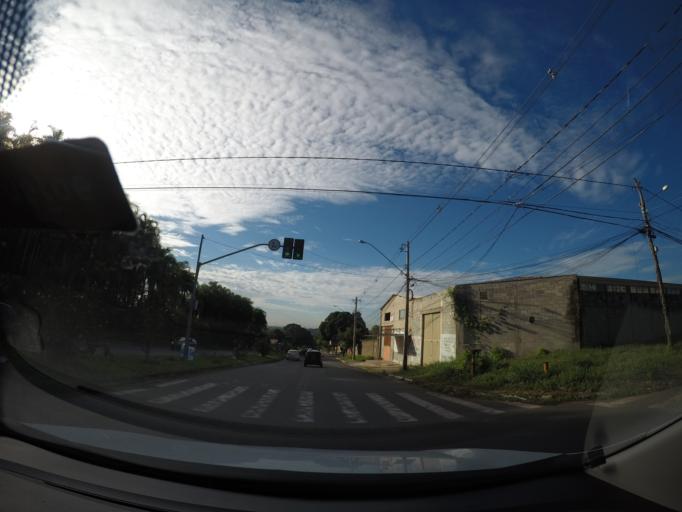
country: BR
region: Goias
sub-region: Goiania
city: Goiania
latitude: -16.7428
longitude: -49.2707
